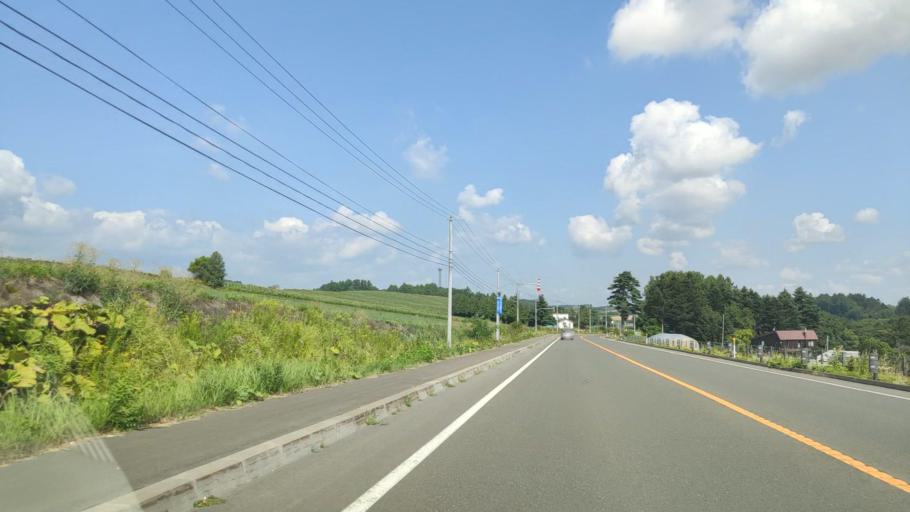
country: JP
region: Hokkaido
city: Shimo-furano
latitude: 43.5229
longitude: 142.4473
